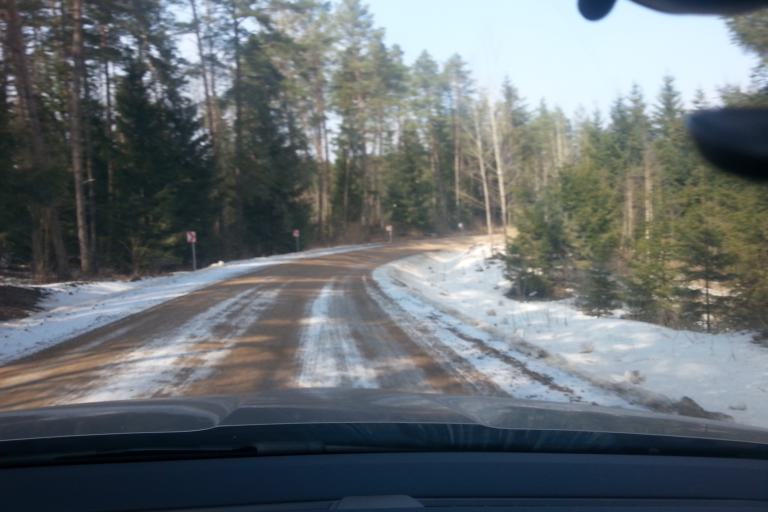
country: LT
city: Trakai
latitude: 54.5682
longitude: 24.9686
